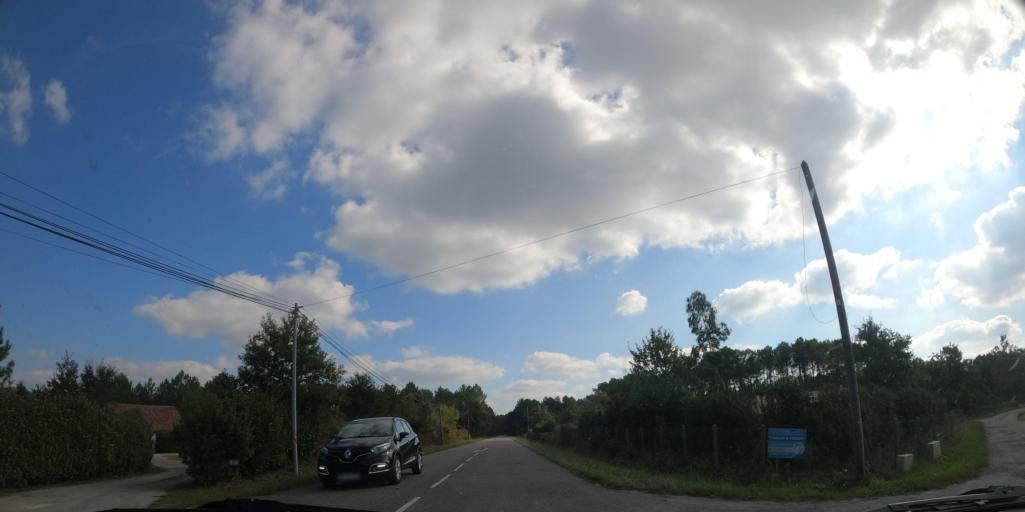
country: FR
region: Aquitaine
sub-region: Departement des Landes
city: Soustons
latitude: 43.7409
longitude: -1.2983
